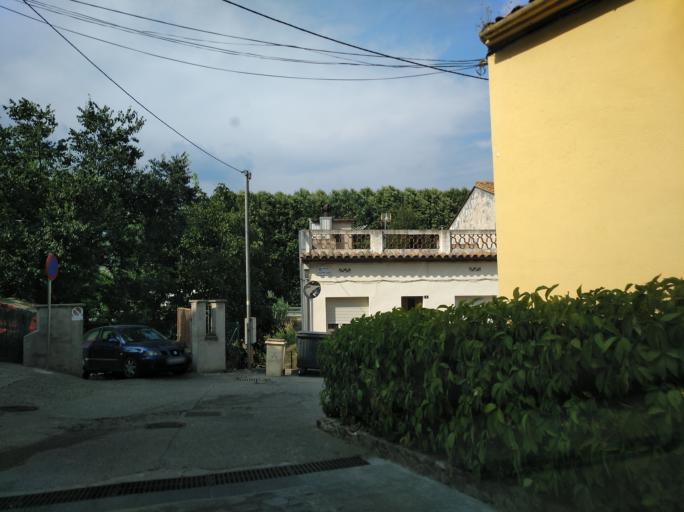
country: ES
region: Catalonia
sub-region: Provincia de Girona
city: Angles
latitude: 41.9578
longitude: 2.6411
